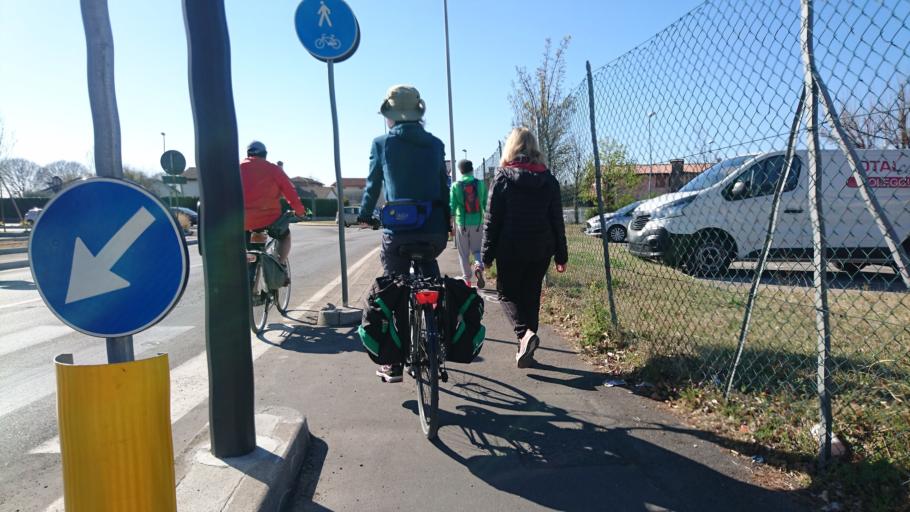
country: IT
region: Veneto
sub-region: Provincia di Vicenza
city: Bassano del Grappa
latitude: 45.7442
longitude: 11.7386
